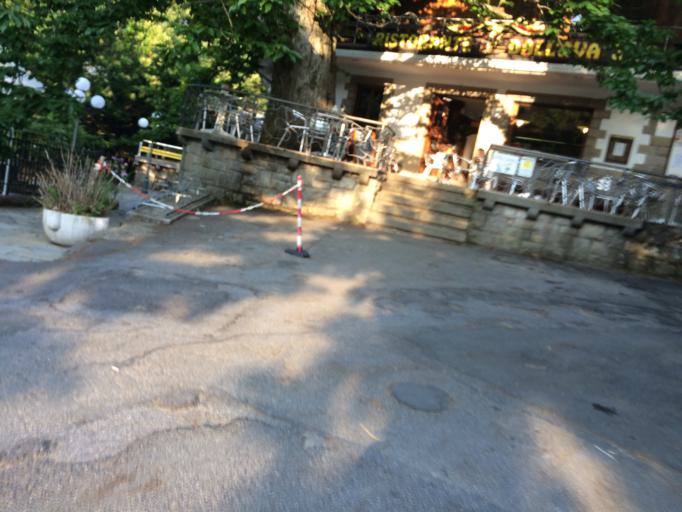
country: IT
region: Liguria
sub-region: Provincia di Imperia
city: Seborga
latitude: 43.8578
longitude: 7.7273
